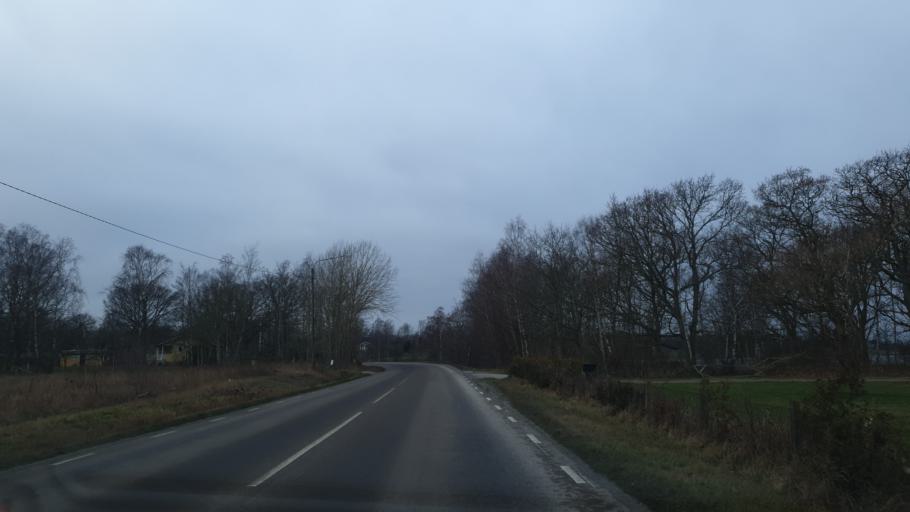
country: SE
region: Blekinge
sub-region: Karlskrona Kommun
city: Sturko
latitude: 56.1107
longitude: 15.7153
